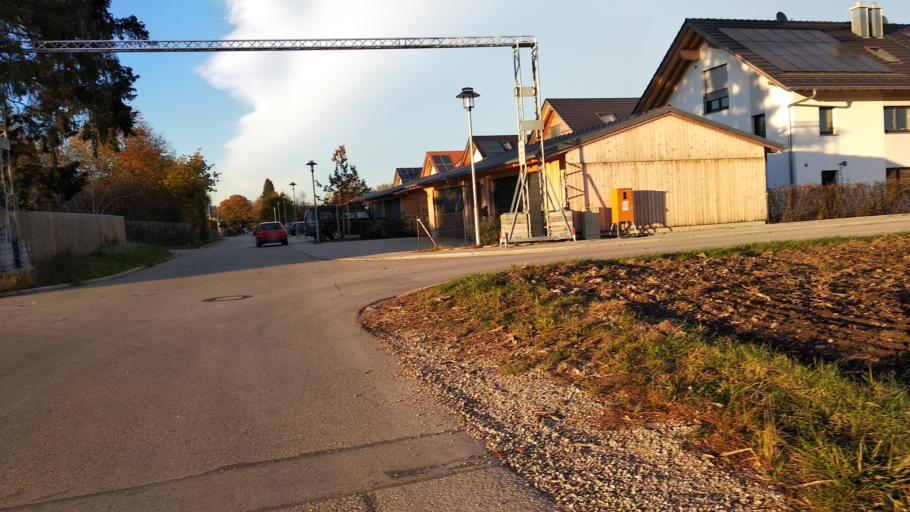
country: DE
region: Bavaria
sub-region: Upper Bavaria
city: Hohenkirchen-Siegertsbrunn
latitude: 48.0214
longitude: 11.7322
